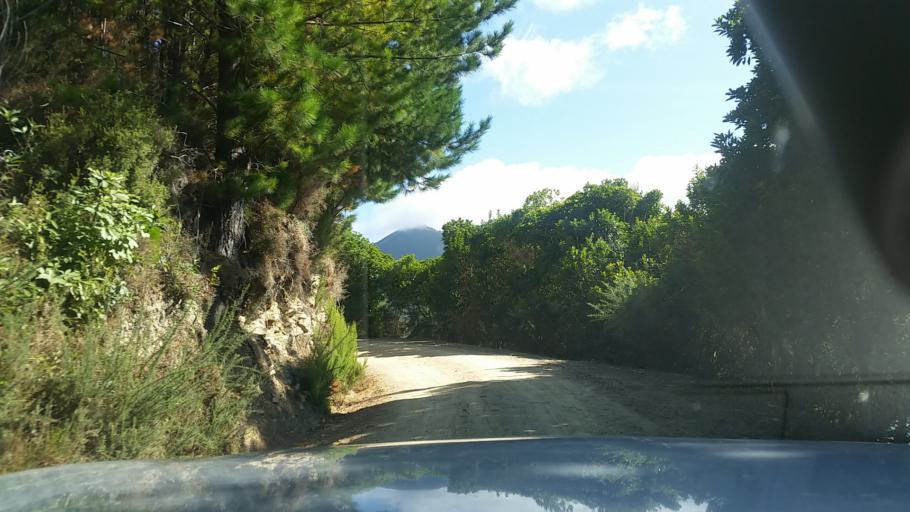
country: NZ
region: Marlborough
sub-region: Marlborough District
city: Picton
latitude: -41.2996
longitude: 174.1855
